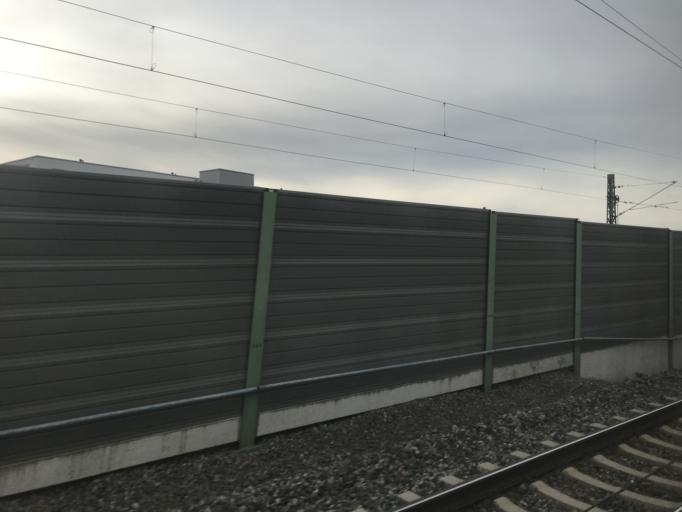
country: DE
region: Bavaria
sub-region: Swabia
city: Mering
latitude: 48.2657
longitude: 10.9834
